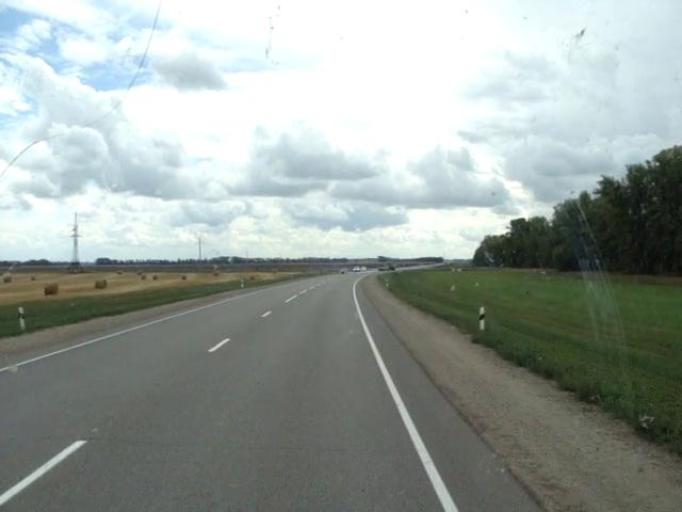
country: RU
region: Altai Krai
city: Shubenka
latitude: 52.6794
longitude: 85.0490
